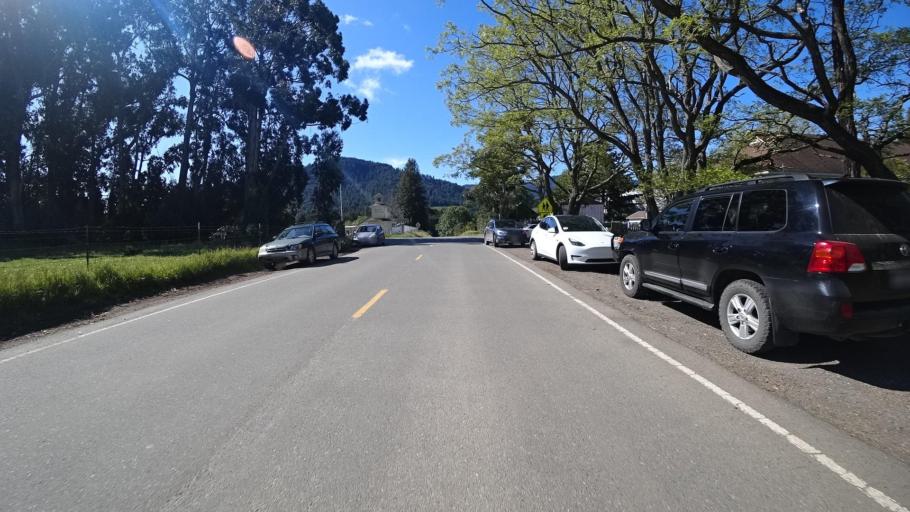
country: US
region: California
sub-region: Humboldt County
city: Rio Dell
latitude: 40.3227
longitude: -124.2859
